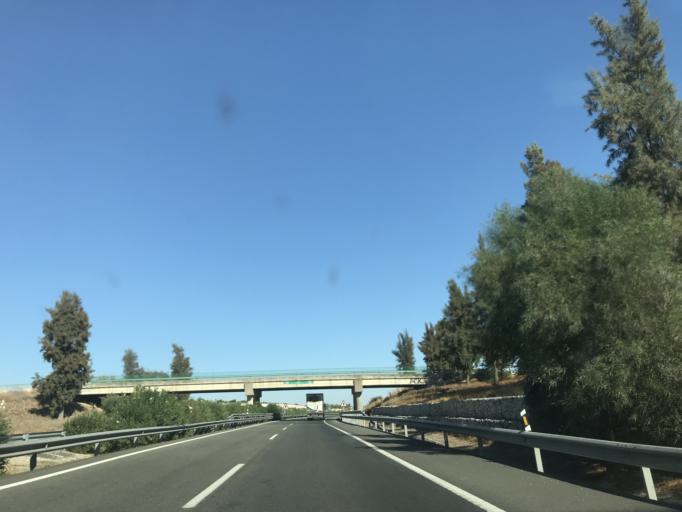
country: ES
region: Andalusia
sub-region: Provincia de Sevilla
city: La Puebla de Cazalla
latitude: 37.2300
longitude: -5.2582
